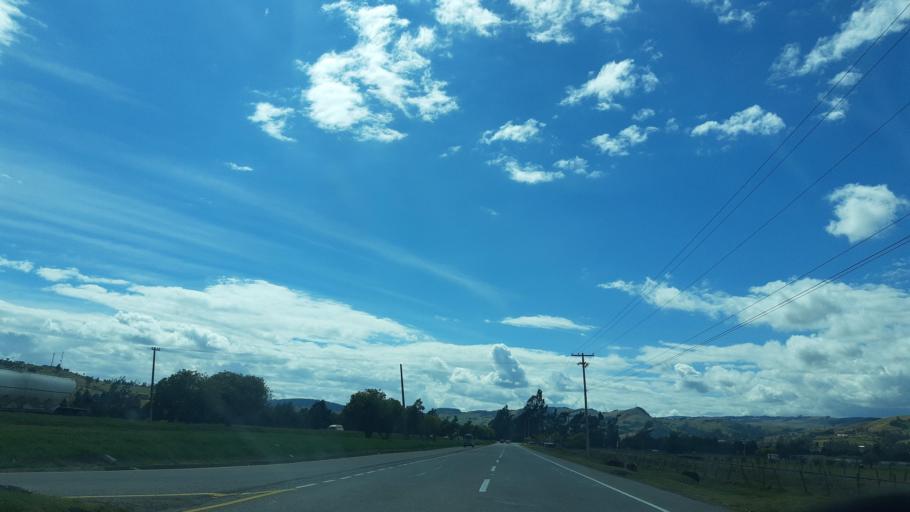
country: CO
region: Cundinamarca
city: Choconta
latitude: 5.1562
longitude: -73.6669
